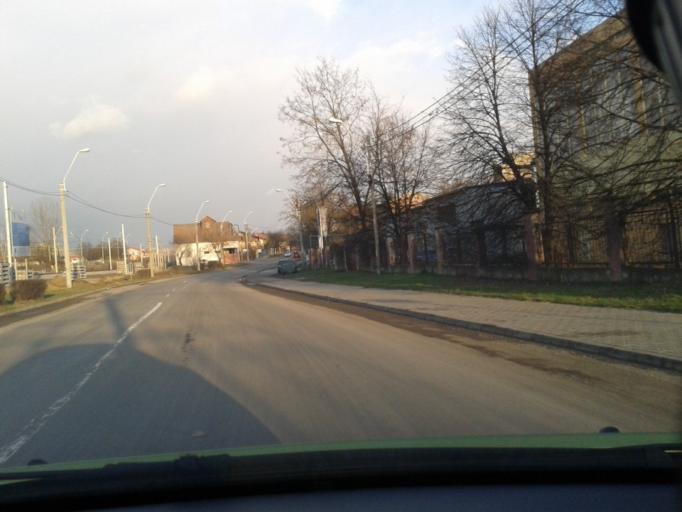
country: RO
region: Sibiu
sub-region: Municipiul Medias
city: Medias
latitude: 46.1698
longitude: 24.3766
